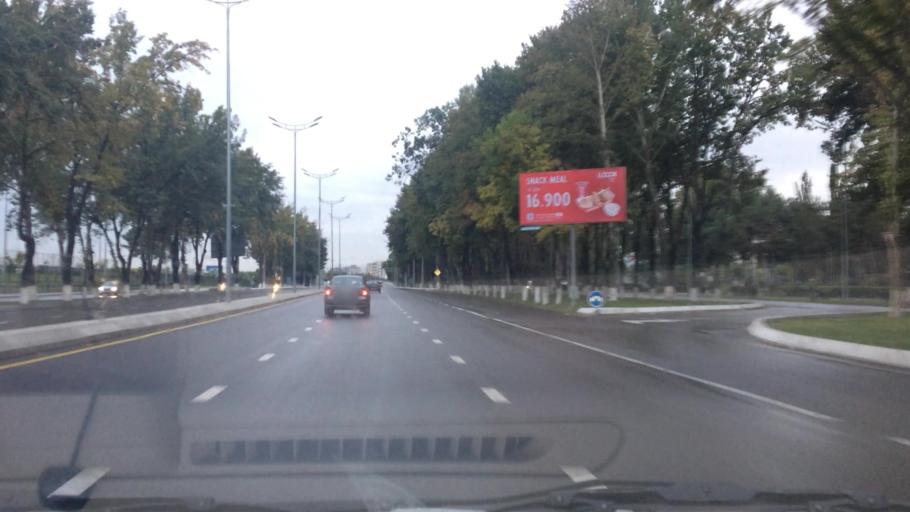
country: UZ
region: Toshkent Shahri
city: Tashkent
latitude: 41.2784
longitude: 69.2081
